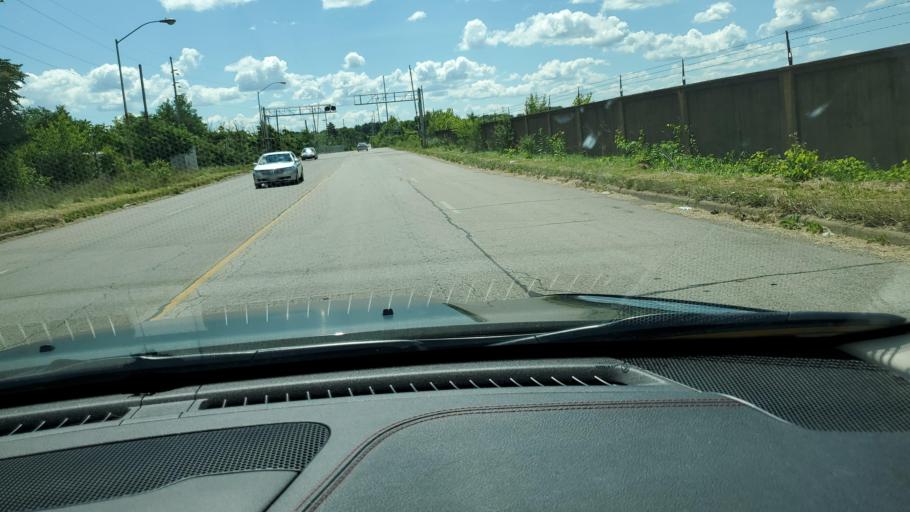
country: US
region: Ohio
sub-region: Trumbull County
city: Warren
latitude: 41.2262
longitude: -80.8113
